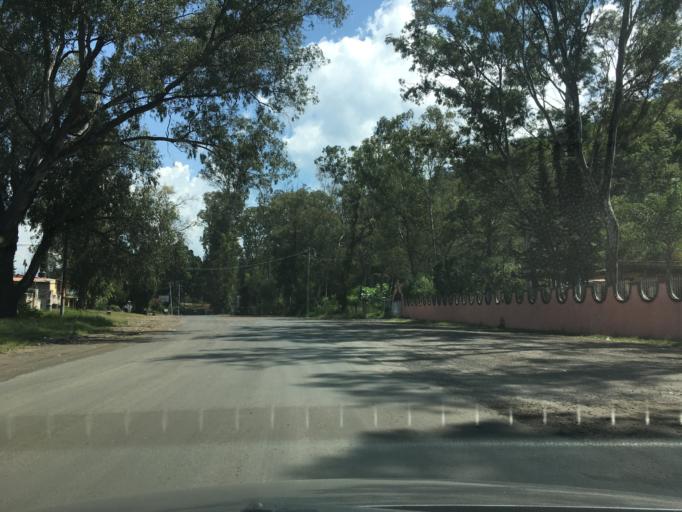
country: MX
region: Michoacan
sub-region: Morelia
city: La Mintzita (Piedra Dura)
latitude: 19.6400
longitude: -101.2768
